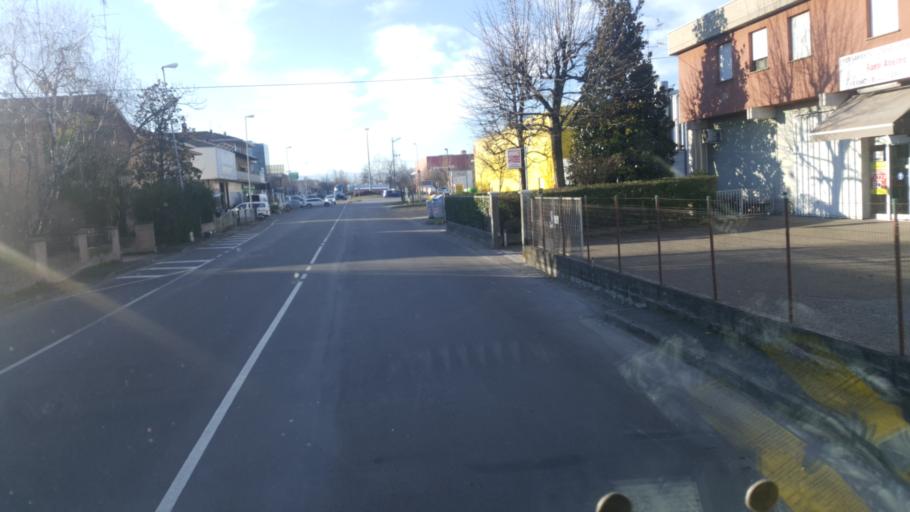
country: IT
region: Emilia-Romagna
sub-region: Provincia di Reggio Emilia
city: Rubiera
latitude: 44.6561
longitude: 10.7740
